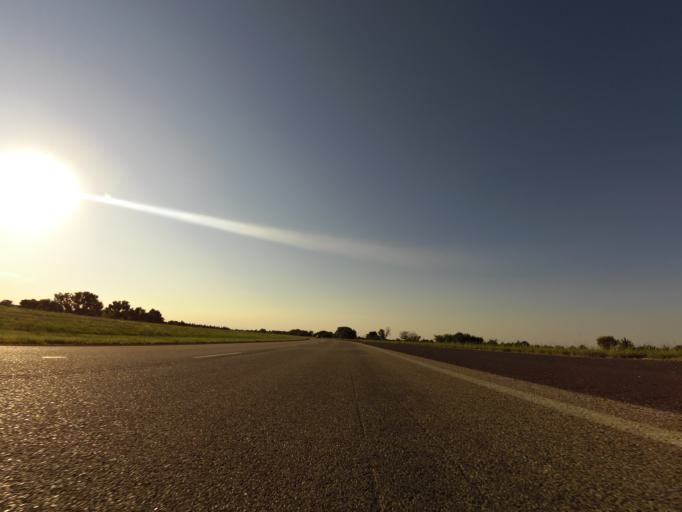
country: US
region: Kansas
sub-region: Reno County
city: South Hutchinson
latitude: 37.9468
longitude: -97.8865
